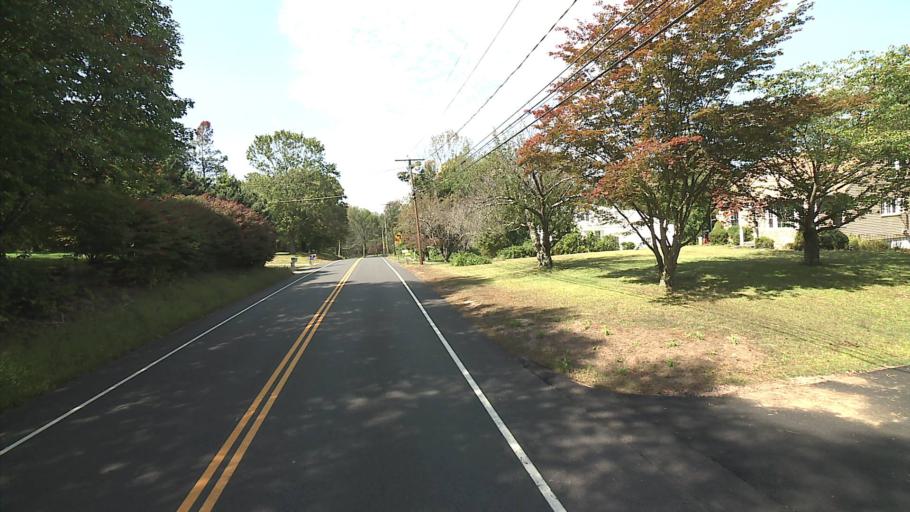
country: US
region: Connecticut
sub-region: Tolland County
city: Coventry Lake
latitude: 41.7184
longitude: -72.3296
